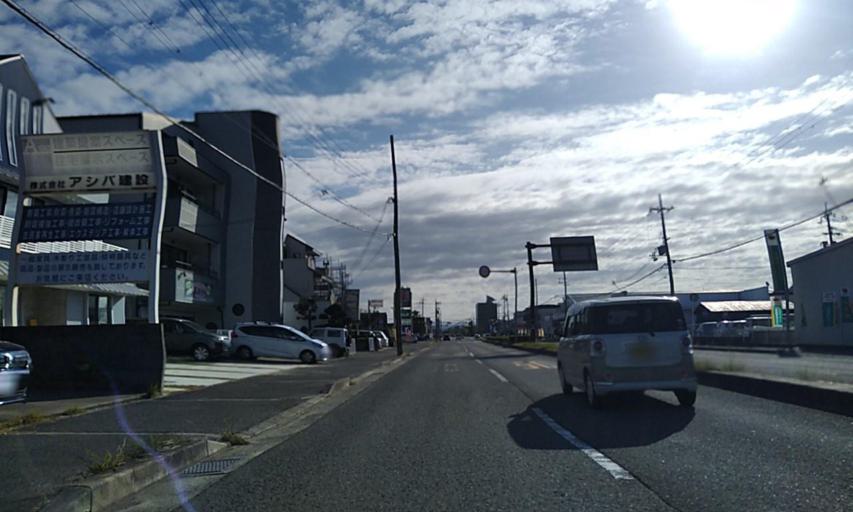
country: JP
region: Wakayama
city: Minato
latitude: 34.2591
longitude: 135.1133
